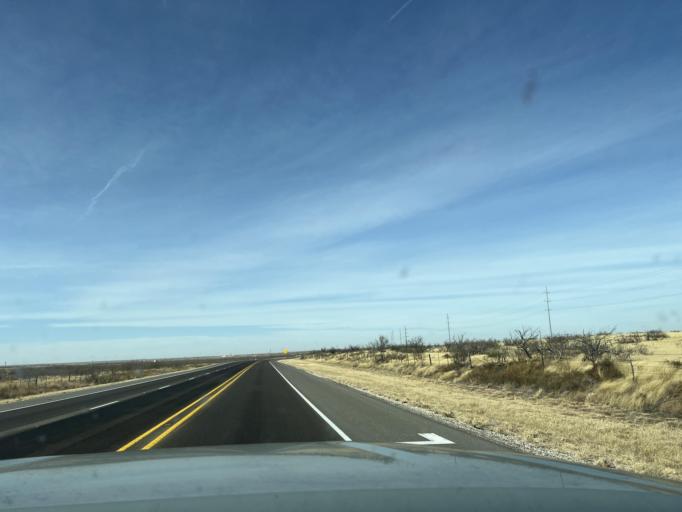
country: US
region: Texas
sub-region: Andrews County
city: Andrews
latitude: 32.3557
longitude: -102.7639
